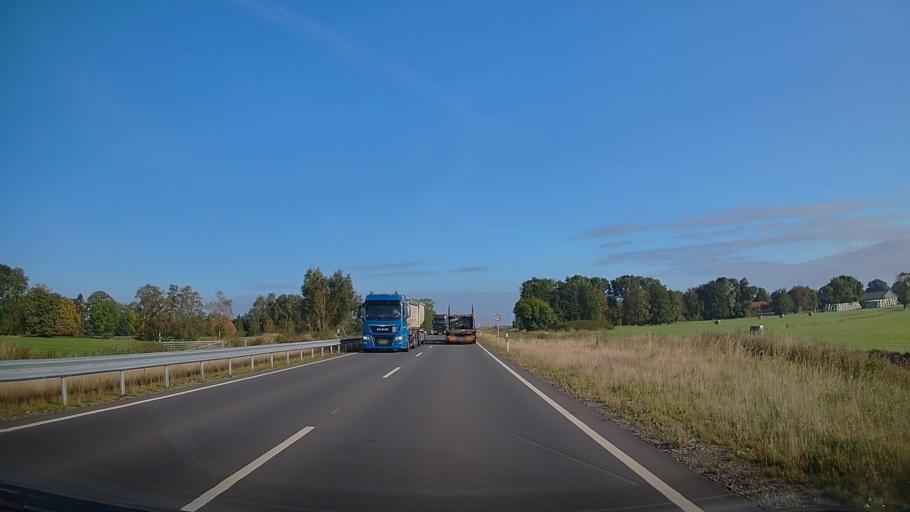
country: DE
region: Lower Saxony
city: Ovelgonne
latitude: 53.3064
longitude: 8.3975
